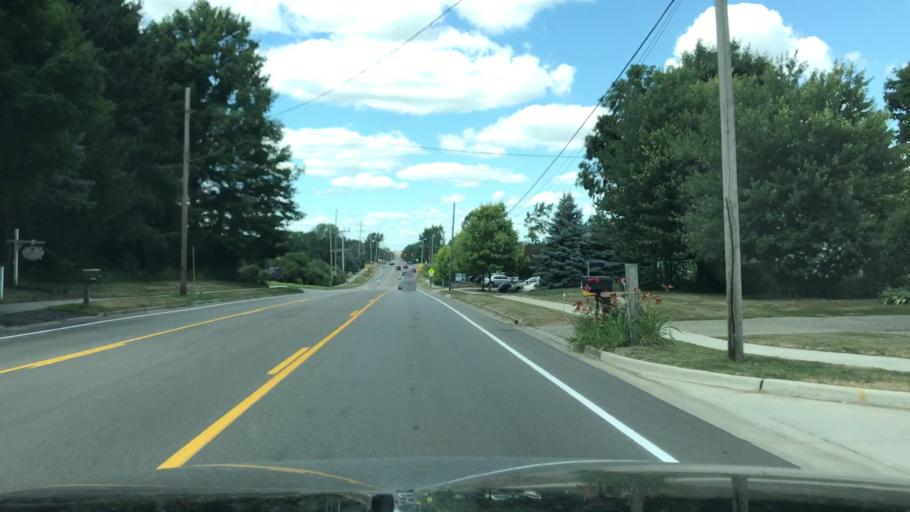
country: US
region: Michigan
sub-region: Kent County
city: Byron Center
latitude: 42.8232
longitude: -85.7230
